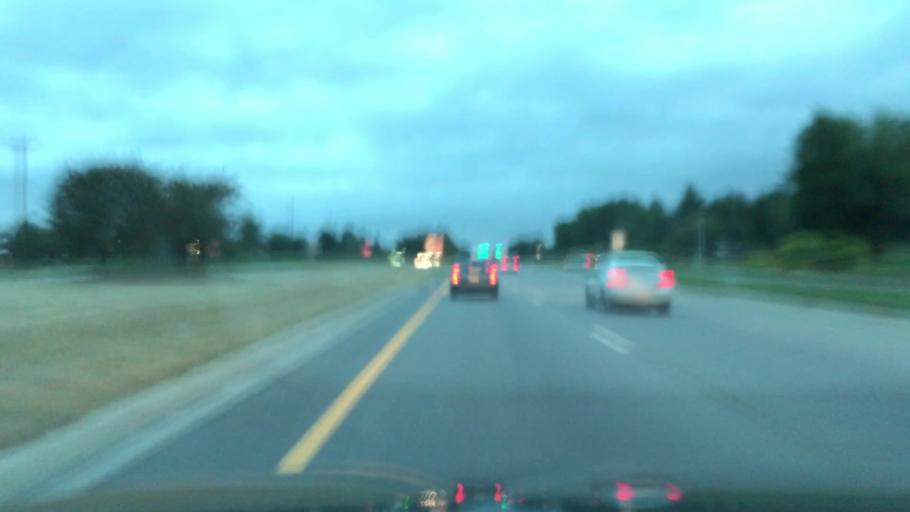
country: US
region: Michigan
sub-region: Kent County
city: East Grand Rapids
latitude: 42.9786
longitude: -85.5905
